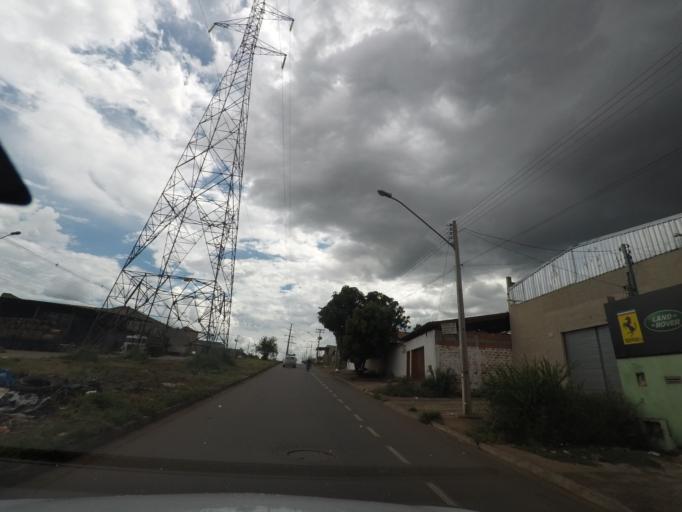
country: BR
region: Goias
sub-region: Goiania
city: Goiania
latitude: -16.7331
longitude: -49.3564
